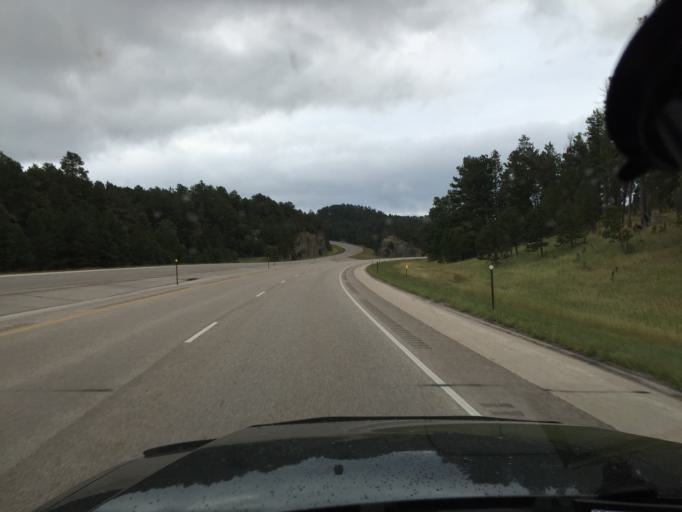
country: US
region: South Dakota
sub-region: Pennington County
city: Colonial Pine Hills
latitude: 43.9433
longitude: -103.3921
